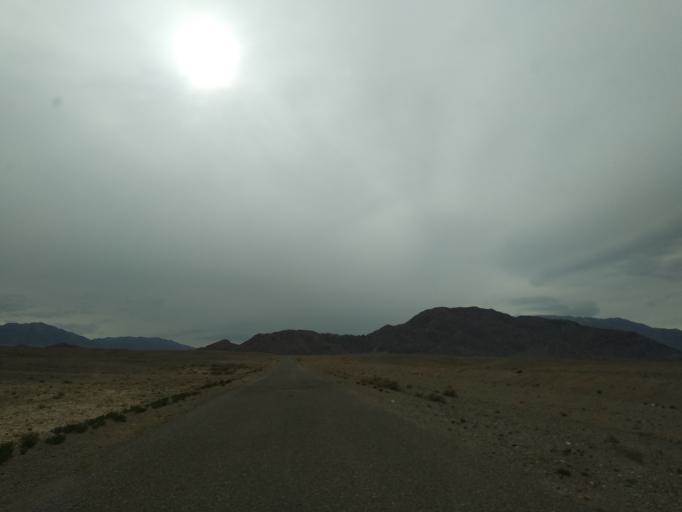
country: KG
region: Ysyk-Koel
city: Balykchy
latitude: 42.3202
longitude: 76.1799
